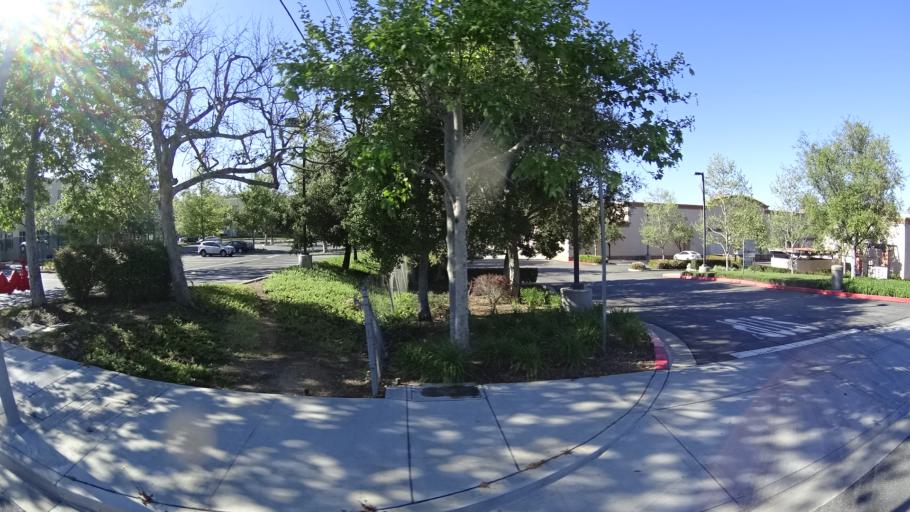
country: US
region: California
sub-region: Ventura County
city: Casa Conejo
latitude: 34.1898
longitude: -118.9333
